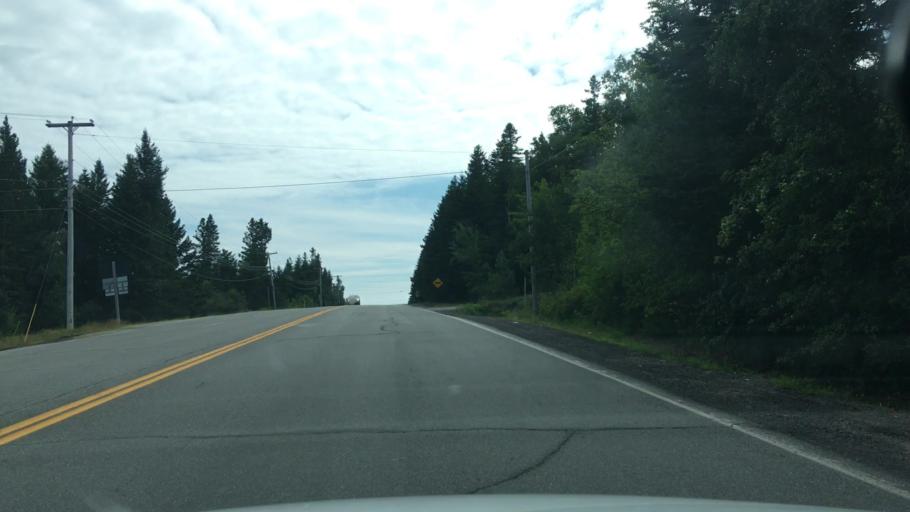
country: CA
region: New Brunswick
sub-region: Charlotte County
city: Saint Andrews
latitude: 44.9703
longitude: -67.0755
